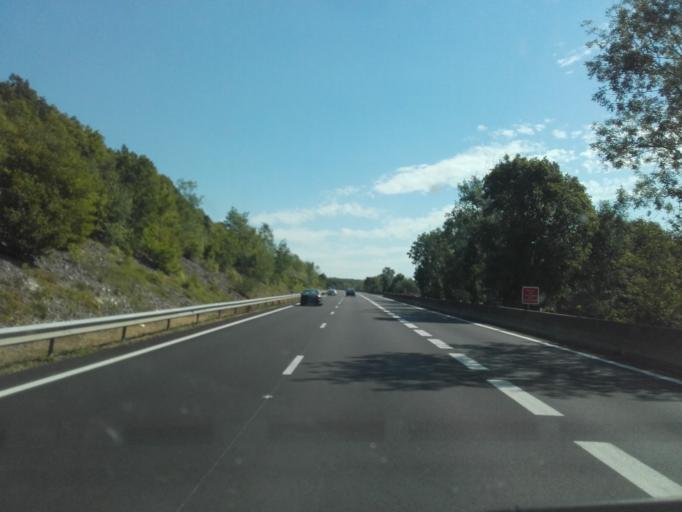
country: FR
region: Bourgogne
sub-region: Departement de la Cote-d'Or
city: Savigny-les-Beaune
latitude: 47.1300
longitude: 4.6990
